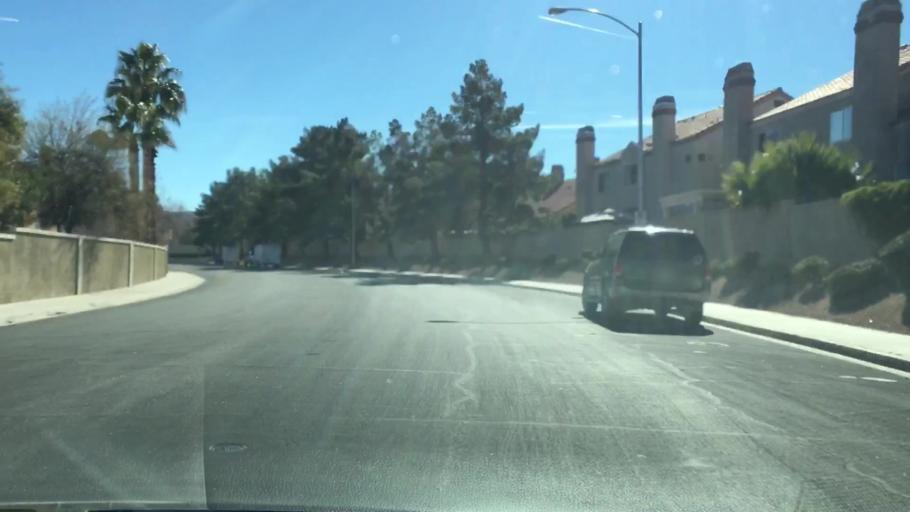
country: US
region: Nevada
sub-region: Clark County
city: Whitney
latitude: 36.0628
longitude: -115.0611
